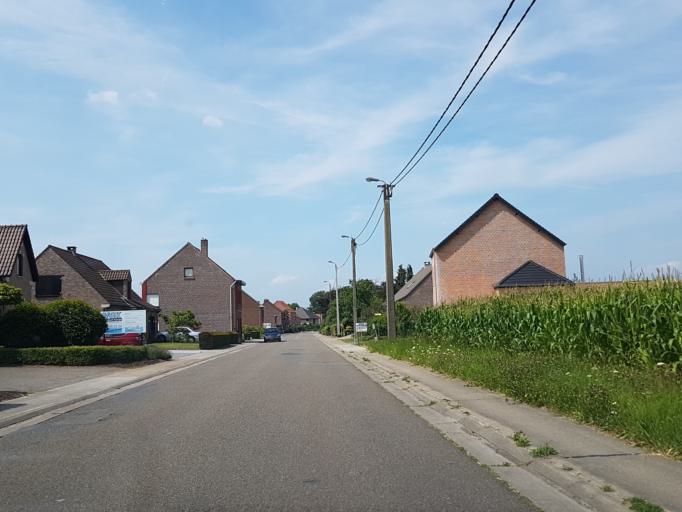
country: BE
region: Flanders
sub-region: Provincie Vlaams-Brabant
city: Kampenhout
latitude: 50.9352
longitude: 4.5658
